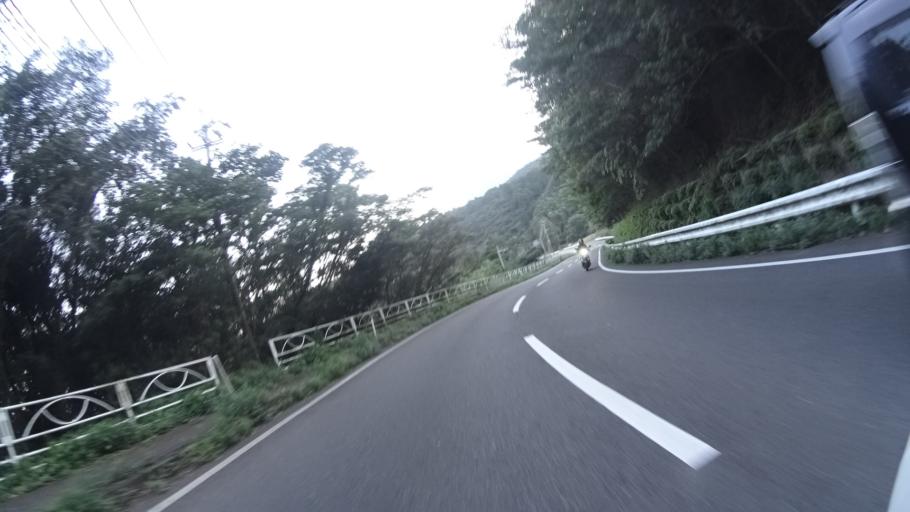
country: JP
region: Oita
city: Beppu
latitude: 33.3275
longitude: 131.4505
